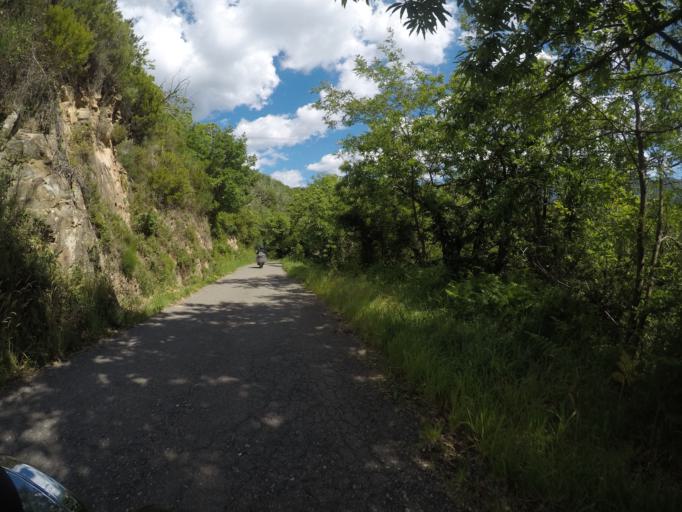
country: IT
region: Tuscany
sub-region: Provincia di Massa-Carrara
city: Casola in Lunigiana
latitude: 44.1791
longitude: 10.1666
